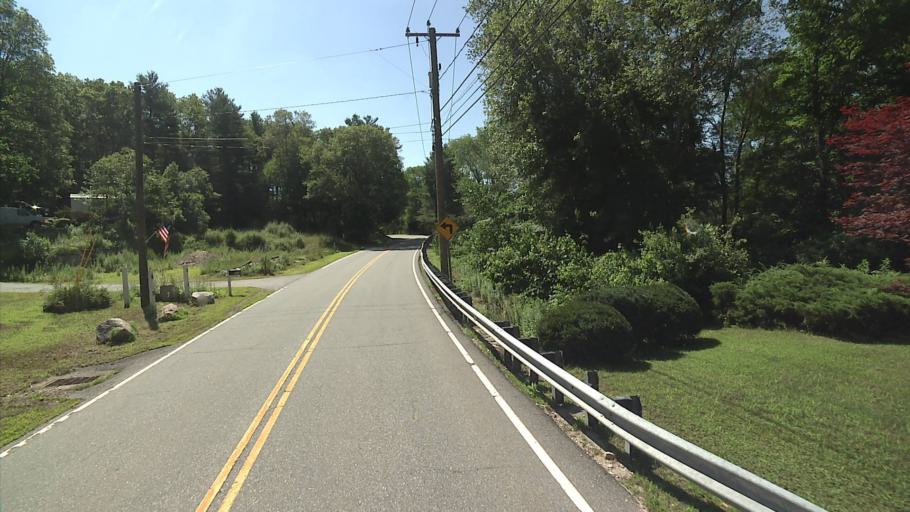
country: US
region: Connecticut
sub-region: Windham County
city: Moosup
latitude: 41.7037
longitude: -71.8209
